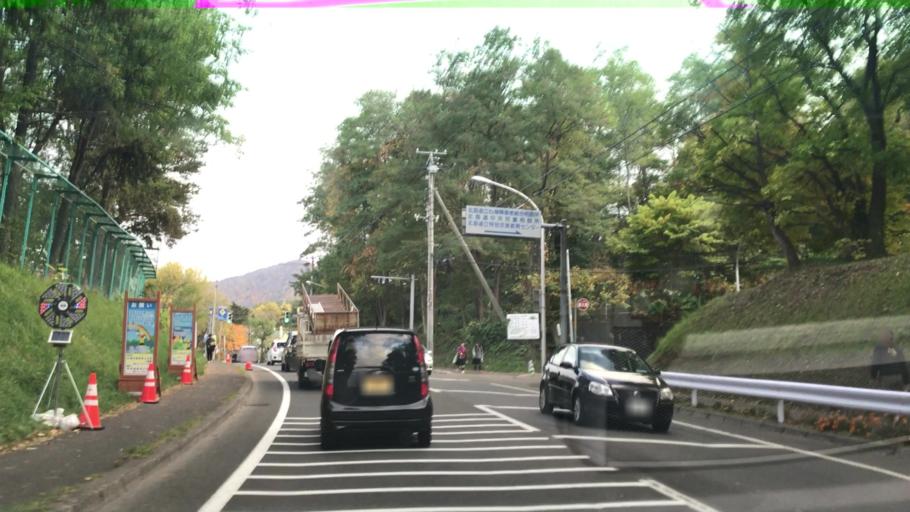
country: JP
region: Hokkaido
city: Sapporo
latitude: 43.0463
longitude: 141.3047
